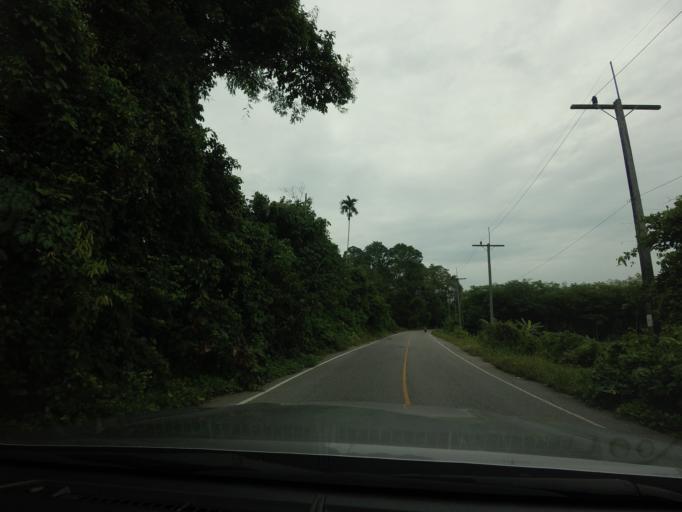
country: TH
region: Narathiwat
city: Rueso
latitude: 6.3525
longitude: 101.4674
